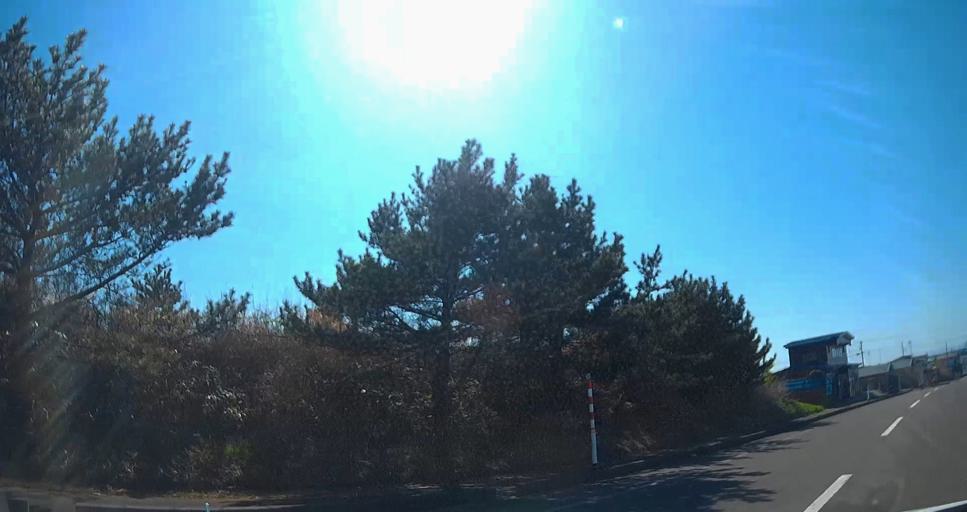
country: JP
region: Hokkaido
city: Hakodate
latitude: 41.5232
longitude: 140.9034
